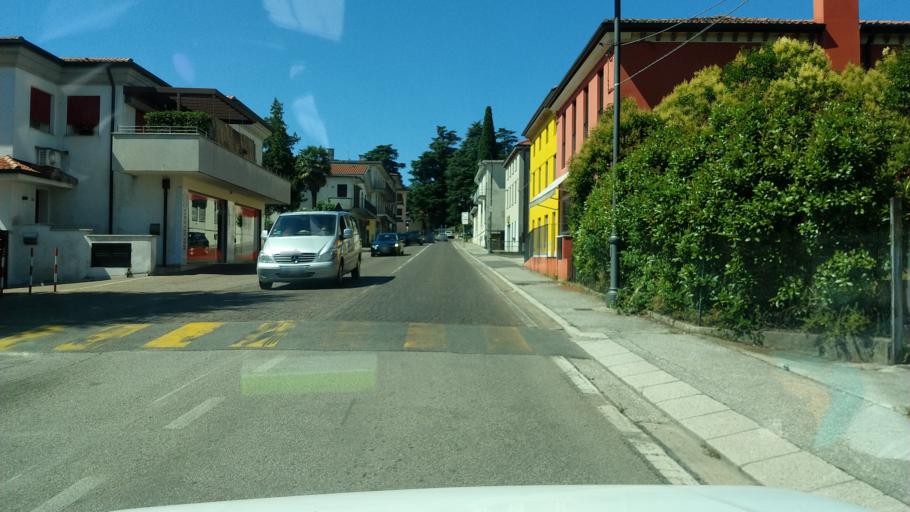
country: IT
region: Veneto
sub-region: Provincia di Vicenza
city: Mason Vicentino
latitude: 45.7190
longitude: 11.6086
